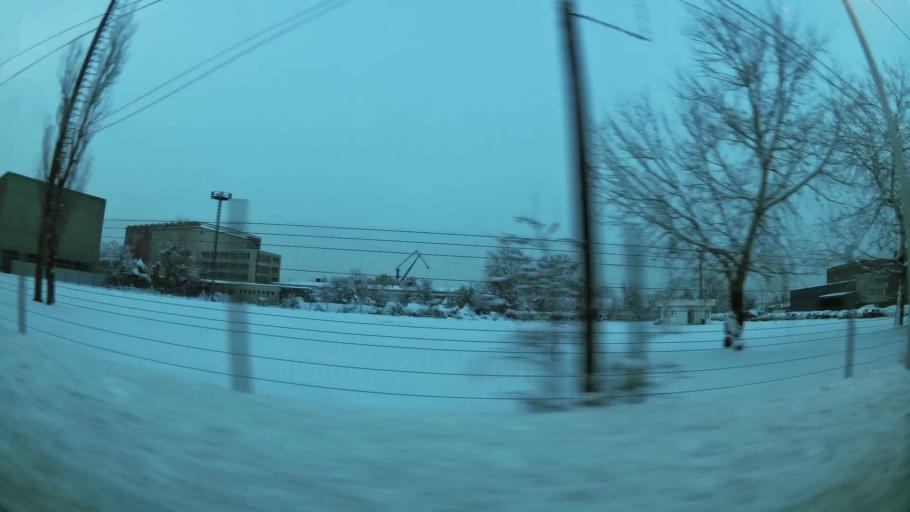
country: RS
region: Central Serbia
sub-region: Belgrade
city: Stari Grad
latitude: 44.8214
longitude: 20.4823
